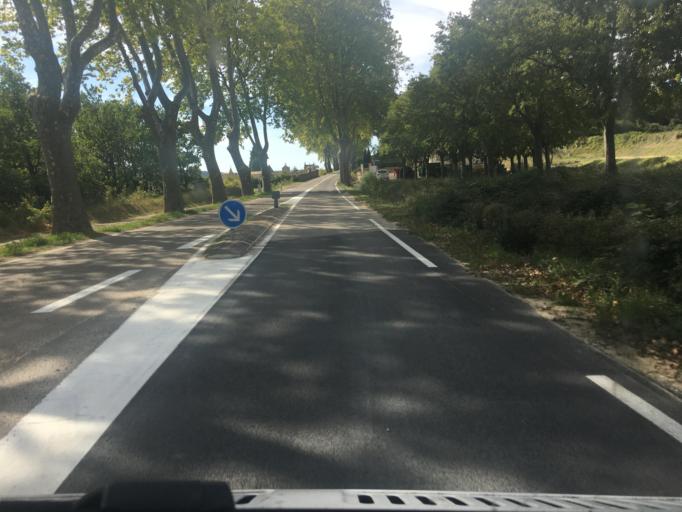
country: FR
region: Languedoc-Roussillon
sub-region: Departement du Gard
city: Saint-Quentin-la-Poterie
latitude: 44.0323
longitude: 4.4892
